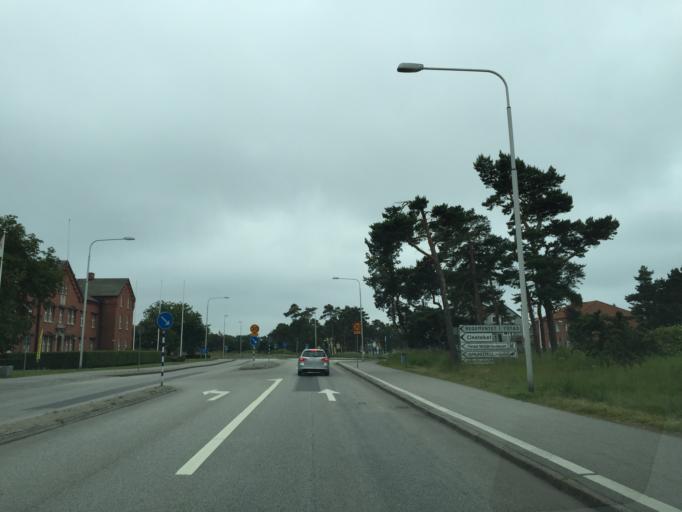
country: SE
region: Skane
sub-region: Ystads Kommun
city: Ystad
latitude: 55.4327
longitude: 13.8390
